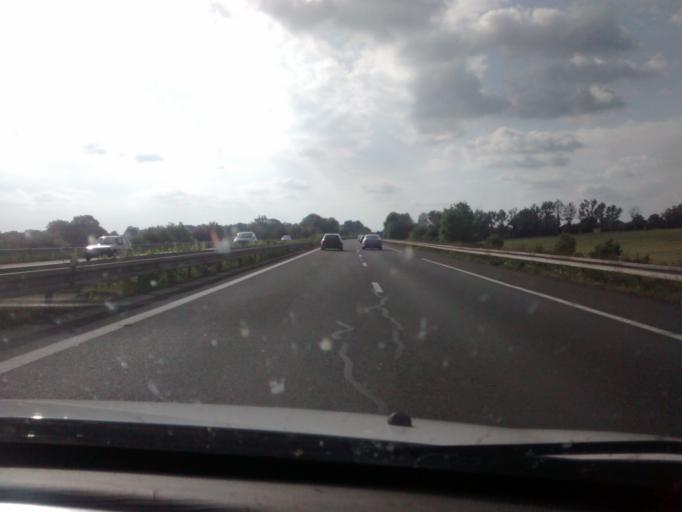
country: FR
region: Pays de la Loire
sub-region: Departement de la Mayenne
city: Argentre
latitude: 48.0825
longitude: -0.6633
